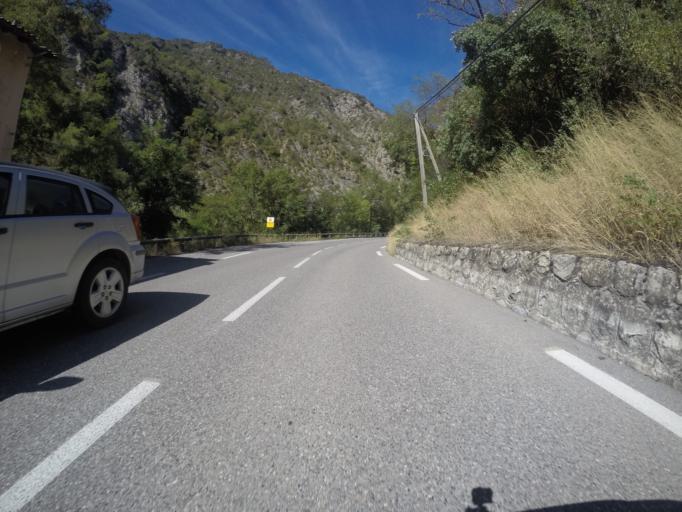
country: FR
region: Provence-Alpes-Cote d'Azur
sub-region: Departement des Alpes-Maritimes
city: Gilette
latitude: 43.9394
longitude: 7.1643
